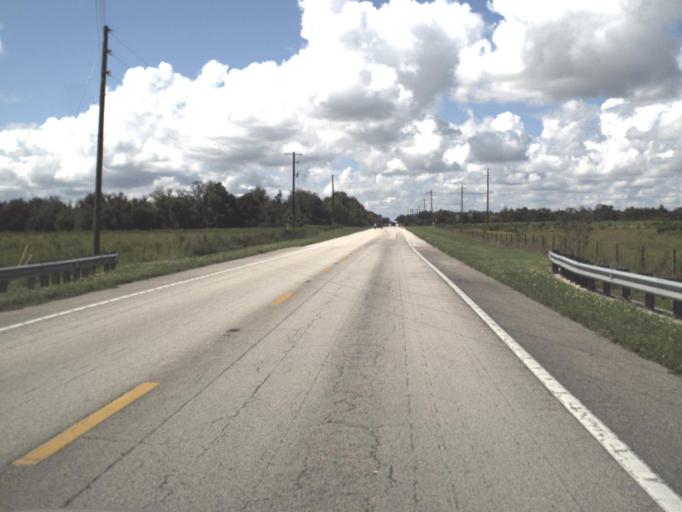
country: US
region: Florida
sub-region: DeSoto County
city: Arcadia
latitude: 27.2575
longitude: -81.9730
